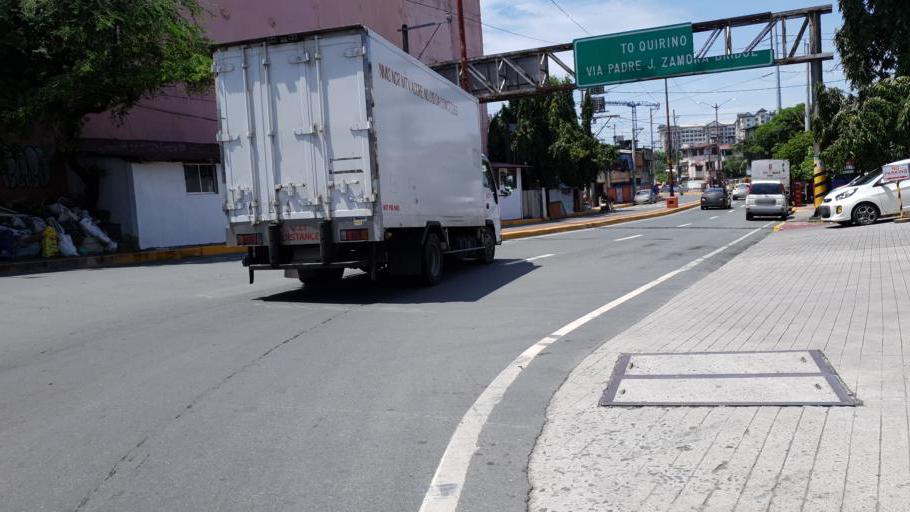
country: PH
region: Metro Manila
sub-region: San Juan
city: San Juan
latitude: 14.5989
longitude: 121.0146
